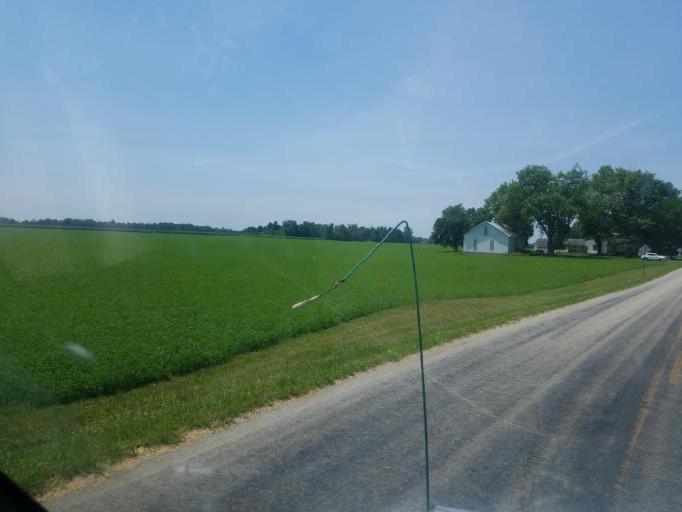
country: US
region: Ohio
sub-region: Shelby County
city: Sidney
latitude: 40.3027
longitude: -84.1168
